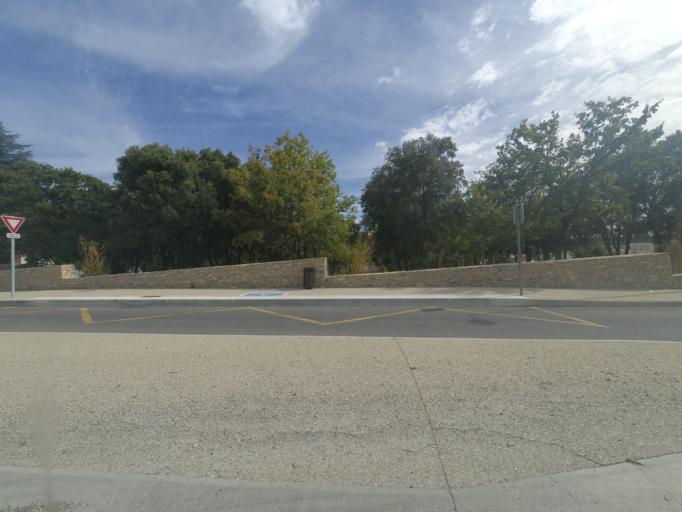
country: FR
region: Languedoc-Roussillon
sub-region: Departement du Gard
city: Nages-et-Solorgues
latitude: 43.7904
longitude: 4.2242
